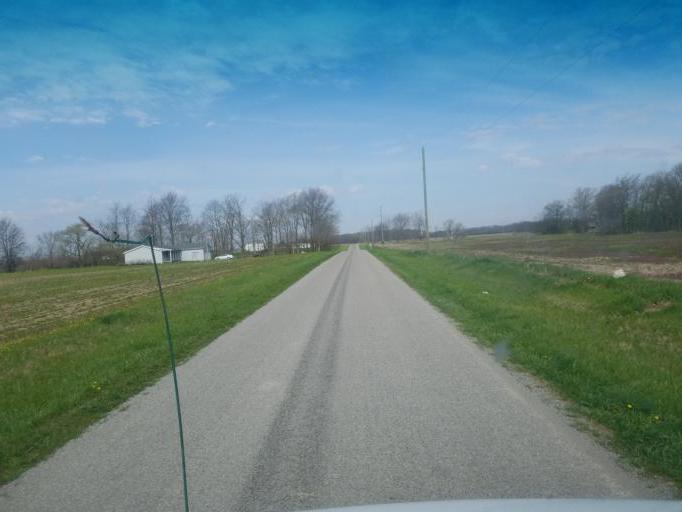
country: US
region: Ohio
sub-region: Union County
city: Richwood
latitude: 40.4837
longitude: -83.4459
